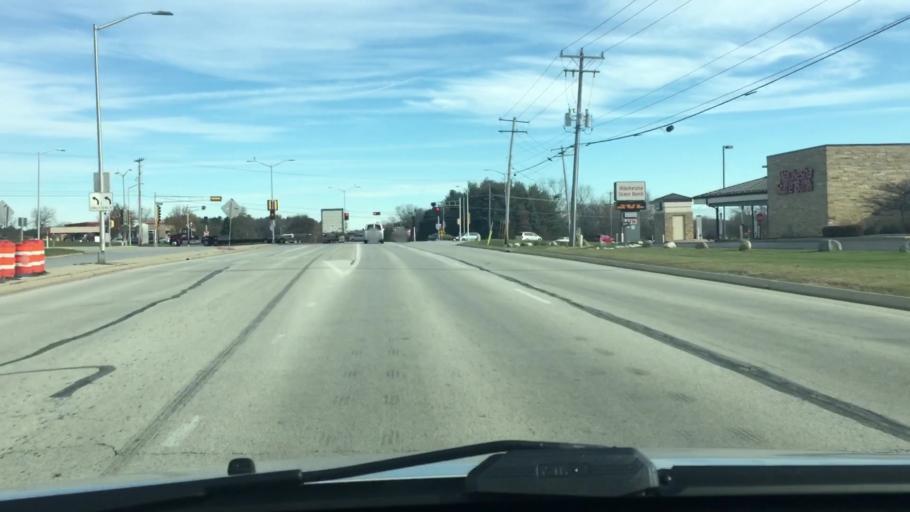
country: US
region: Wisconsin
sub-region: Waukesha County
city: Waukesha
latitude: 42.9874
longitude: -88.2679
